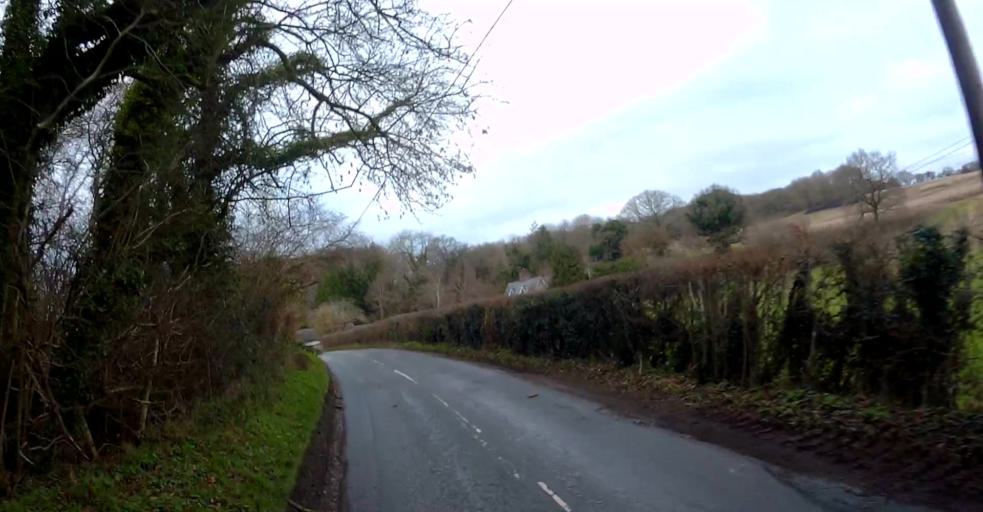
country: GB
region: England
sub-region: Hampshire
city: Basingstoke
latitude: 51.1890
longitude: -1.1447
